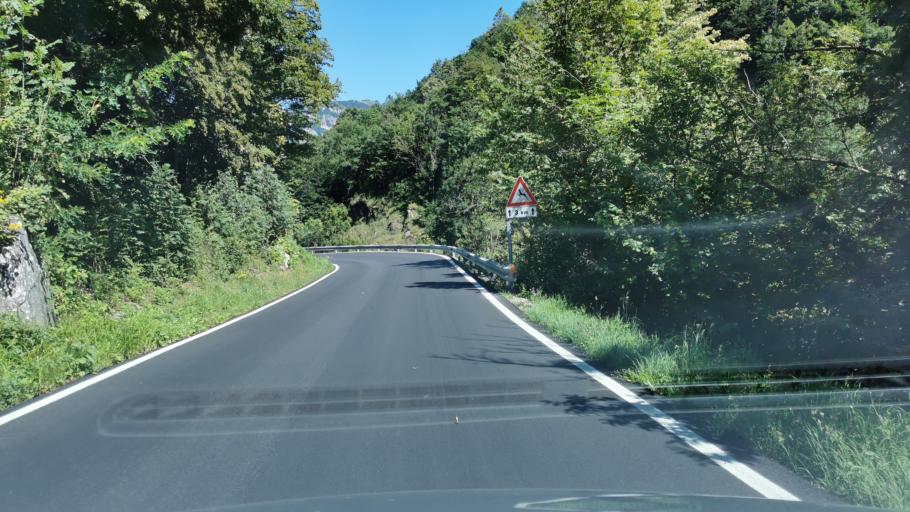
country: IT
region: Piedmont
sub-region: Provincia di Cuneo
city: Entracque
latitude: 44.2531
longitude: 7.3473
